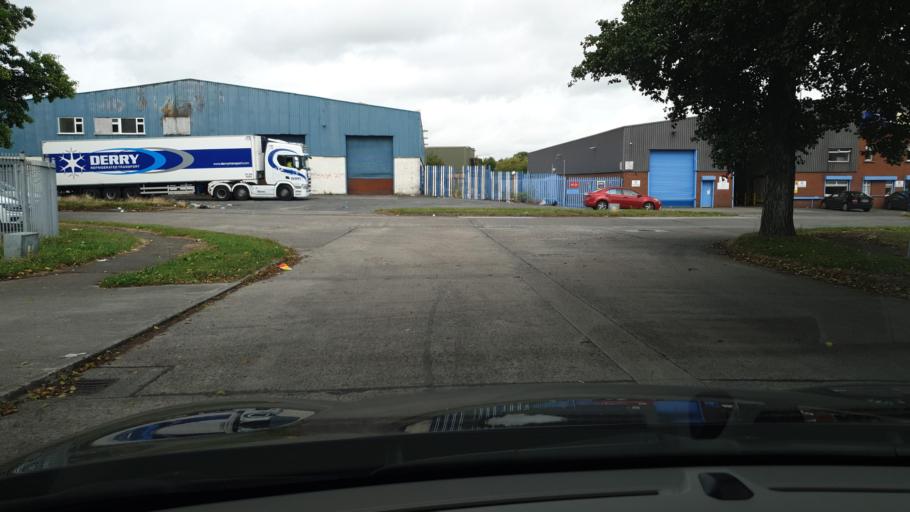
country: IE
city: Palmerstown
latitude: 53.3466
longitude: -6.3777
